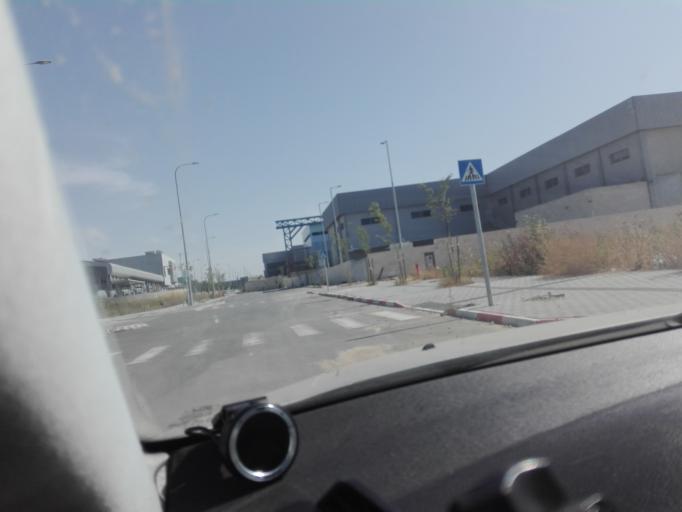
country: IL
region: Central District
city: Bene 'Ayish
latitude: 31.7263
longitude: 34.7600
